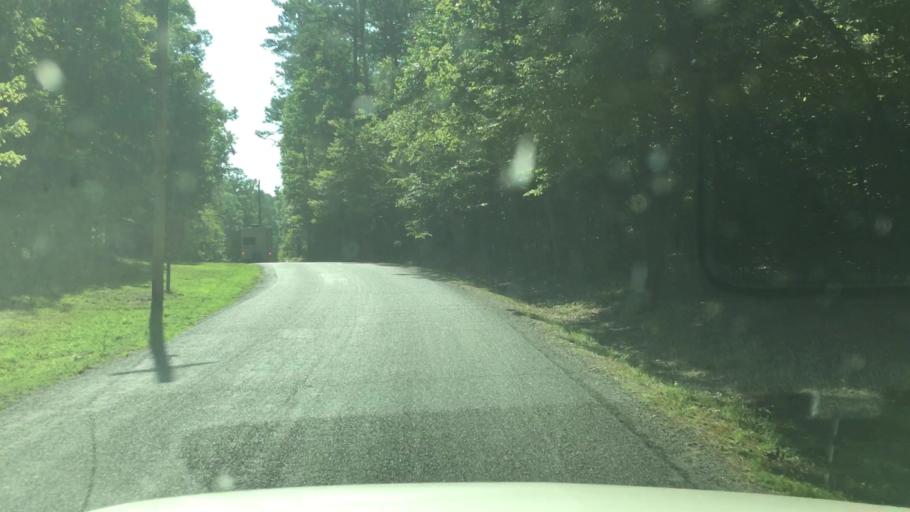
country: US
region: Arkansas
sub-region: Garland County
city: Piney
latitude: 34.5402
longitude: -93.3460
